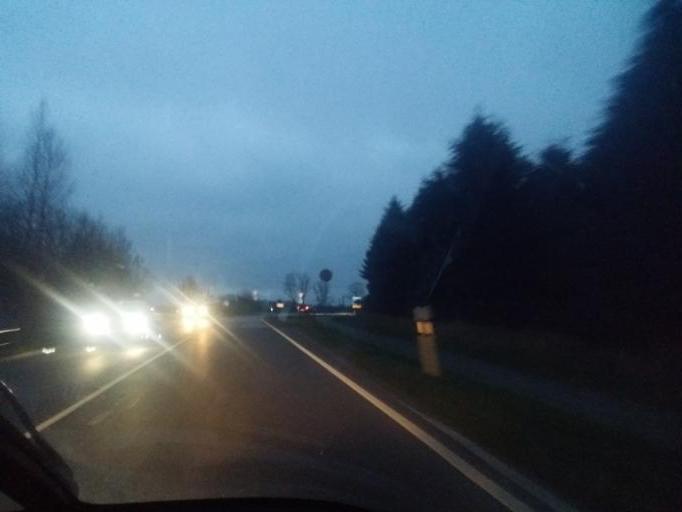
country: DE
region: Schleswig-Holstein
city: Poschendorf
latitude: 54.0334
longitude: 9.4784
